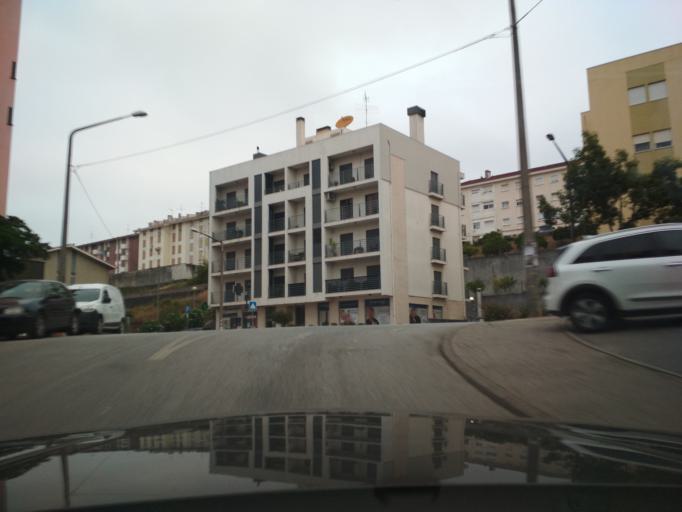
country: PT
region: Coimbra
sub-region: Coimbra
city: Coimbra
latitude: 40.1957
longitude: -8.4148
